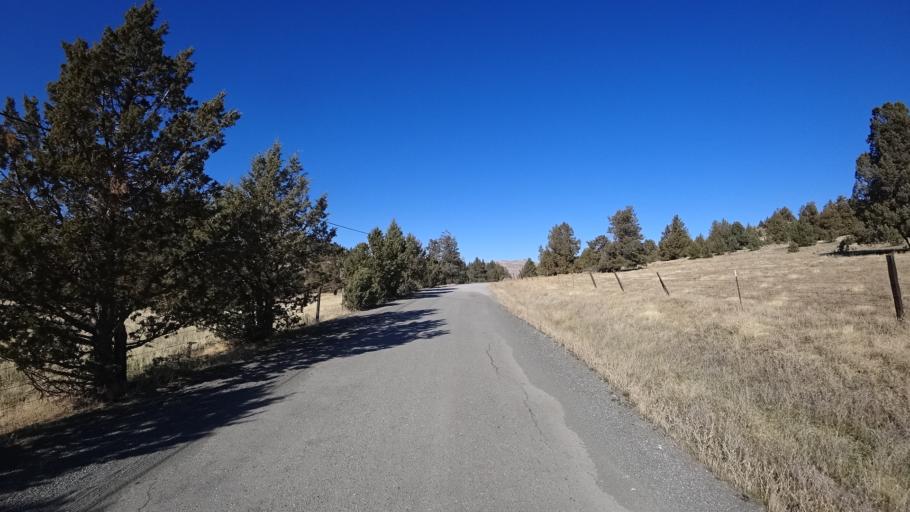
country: US
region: California
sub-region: Siskiyou County
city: Montague
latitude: 41.8022
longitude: -122.3697
